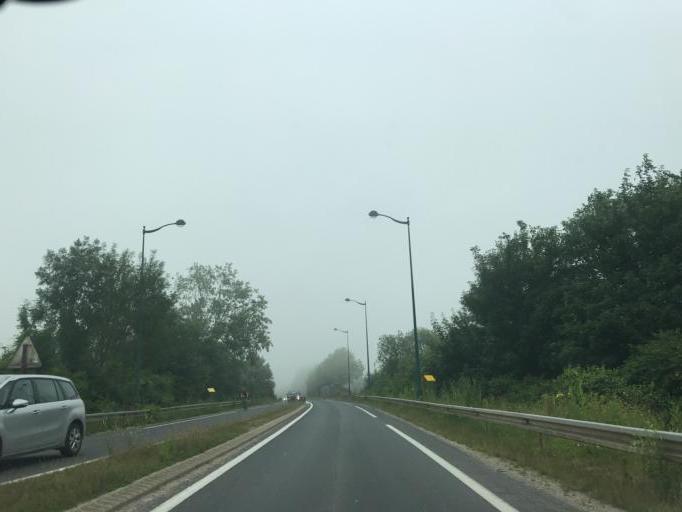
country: FR
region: Ile-de-France
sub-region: Departement de Seine-et-Marne
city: Chalifert
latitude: 48.8809
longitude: 2.7824
